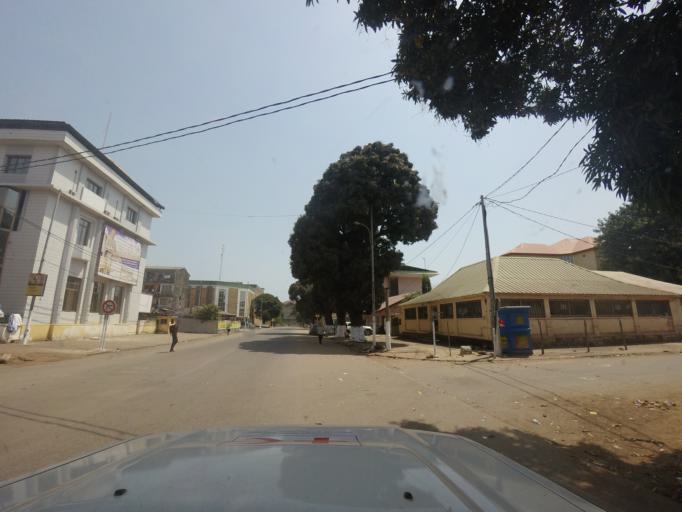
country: GN
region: Conakry
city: Camayenne
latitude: 9.5090
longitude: -13.7151
